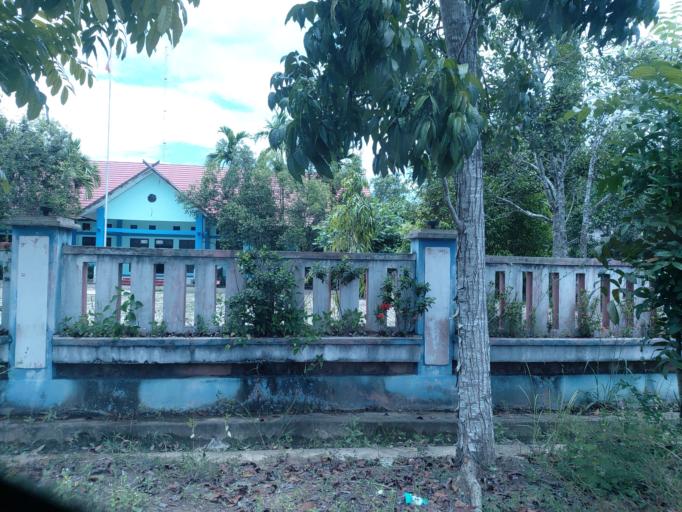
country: ID
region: Central Kalimantan
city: Tamianglayang
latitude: -2.0717
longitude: 115.1396
